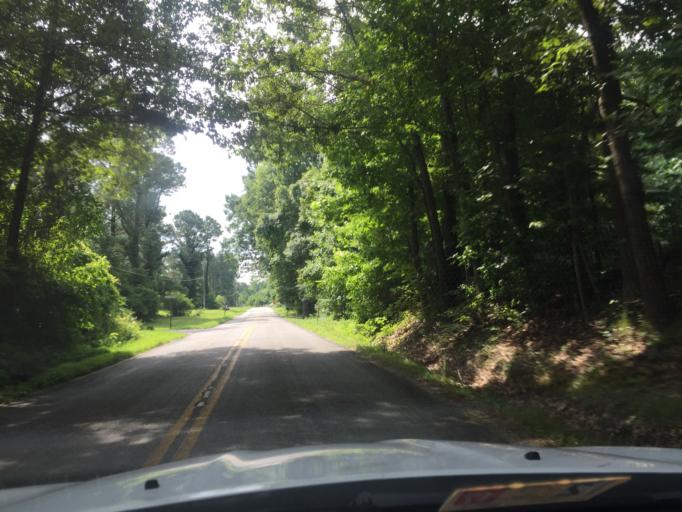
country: US
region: Virginia
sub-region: Charles City County
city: Charles City
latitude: 37.4053
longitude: -77.0252
